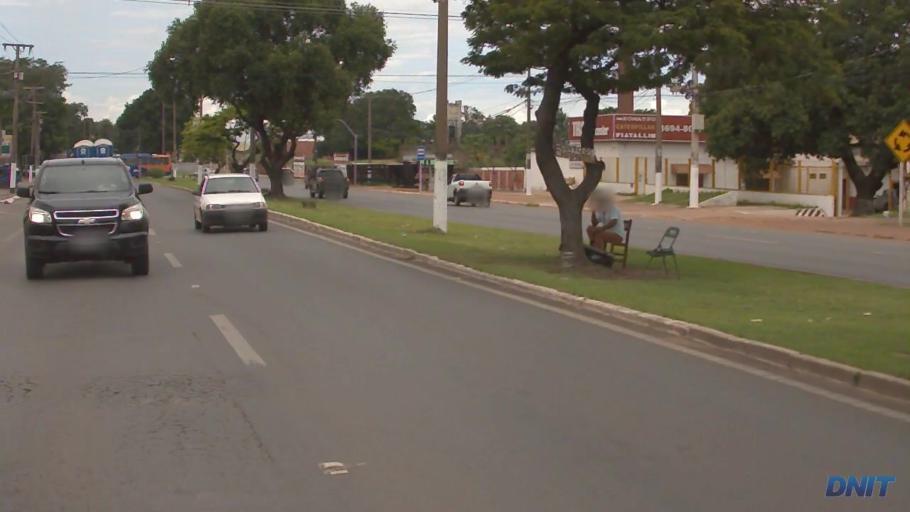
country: BR
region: Mato Grosso
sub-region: Varzea Grande
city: Varzea Grande
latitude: -15.6433
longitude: -56.1597
